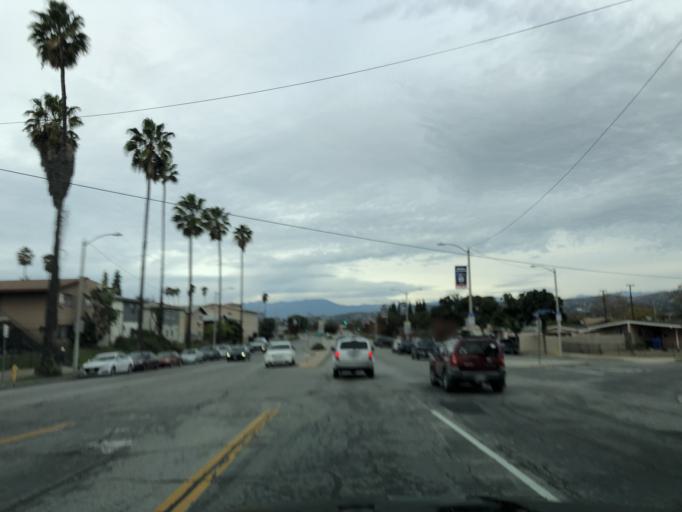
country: US
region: California
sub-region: Los Angeles County
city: South Whittier
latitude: 33.9416
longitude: -118.0465
